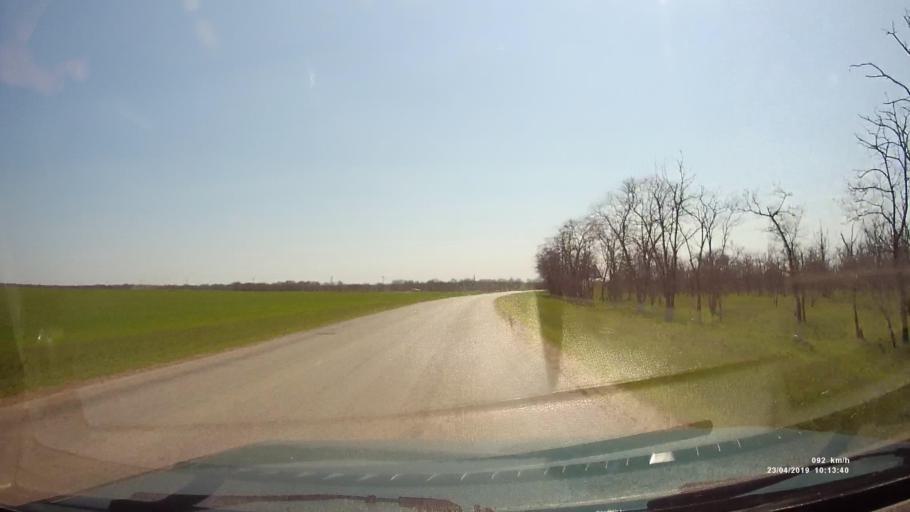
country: RU
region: Rostov
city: Sovetskoye
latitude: 46.6837
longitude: 42.3595
